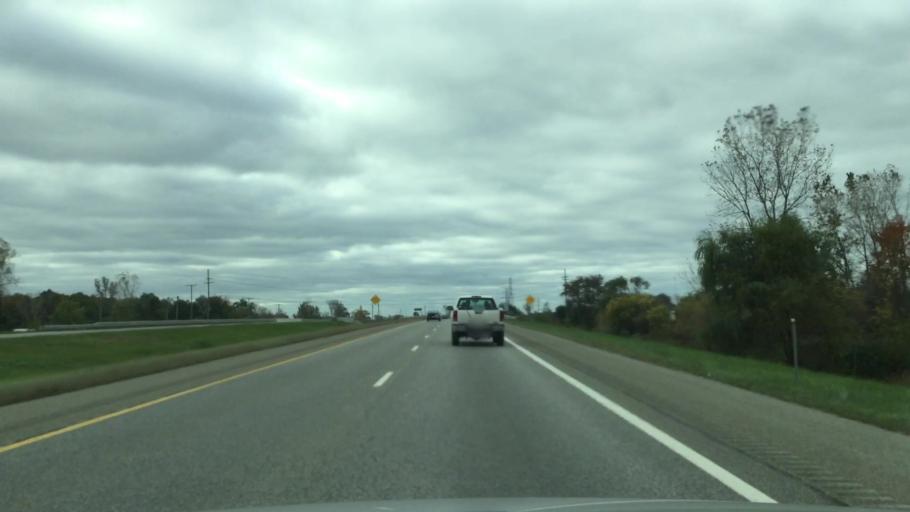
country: US
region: Michigan
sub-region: Macomb County
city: Romeo
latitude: 42.7893
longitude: -83.0045
